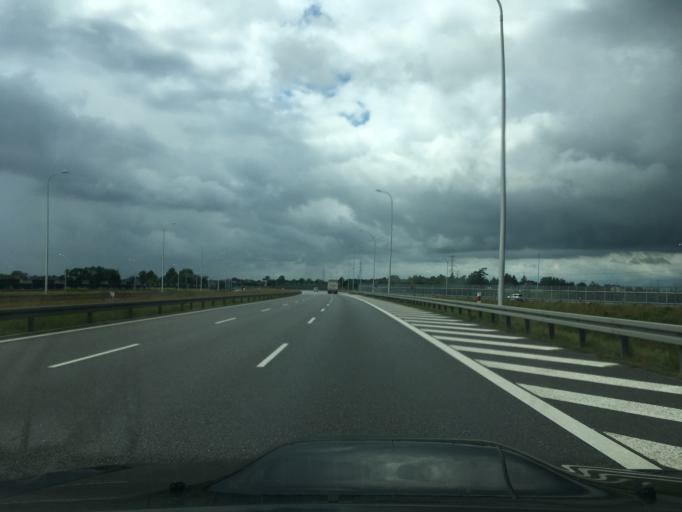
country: PL
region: Lublin Voivodeship
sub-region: Powiat lubelski
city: Lublin
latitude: 51.3027
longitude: 22.5852
